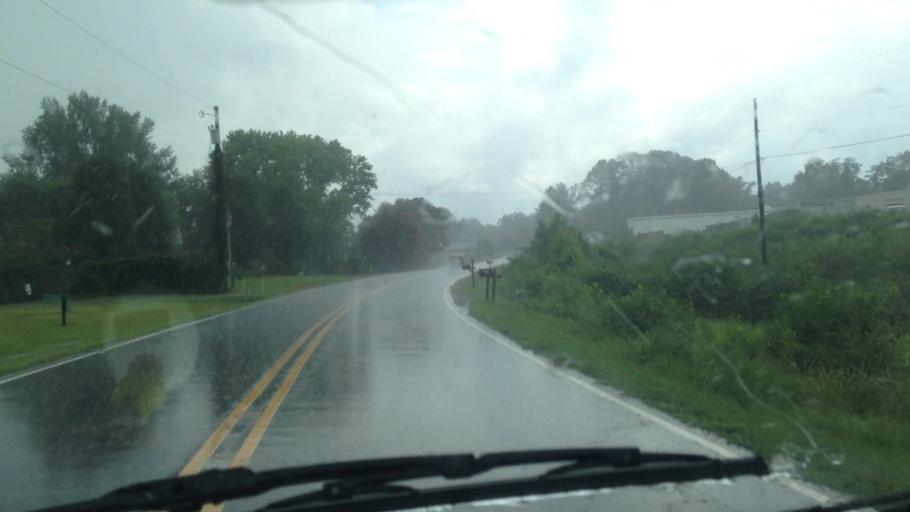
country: US
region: North Carolina
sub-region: Stokes County
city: Danbury
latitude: 36.4068
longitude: -80.0924
